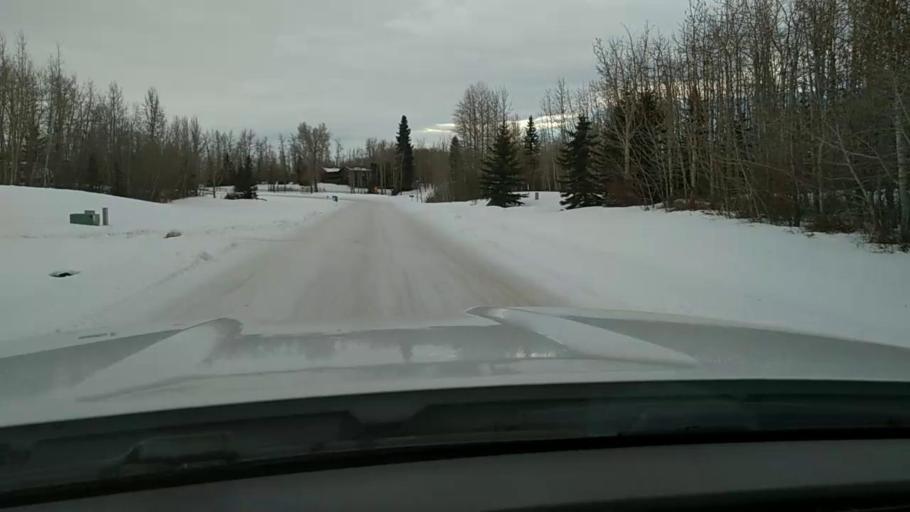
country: CA
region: Alberta
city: Cochrane
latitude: 51.1817
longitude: -114.2559
